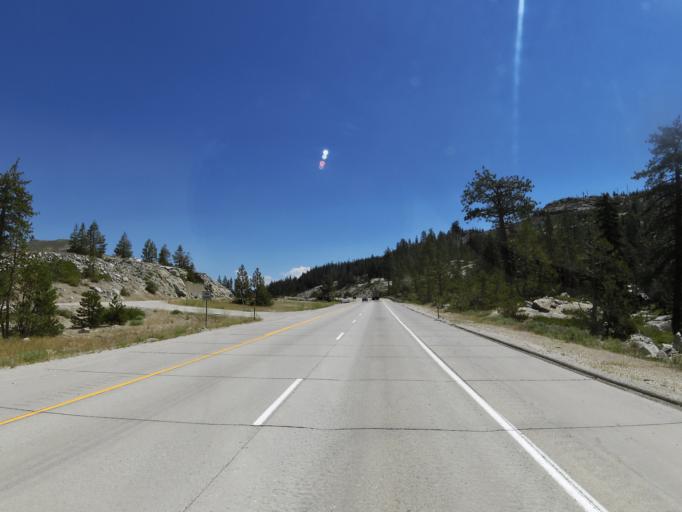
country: US
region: California
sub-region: Nevada County
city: Truckee
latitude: 39.3136
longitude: -120.4726
